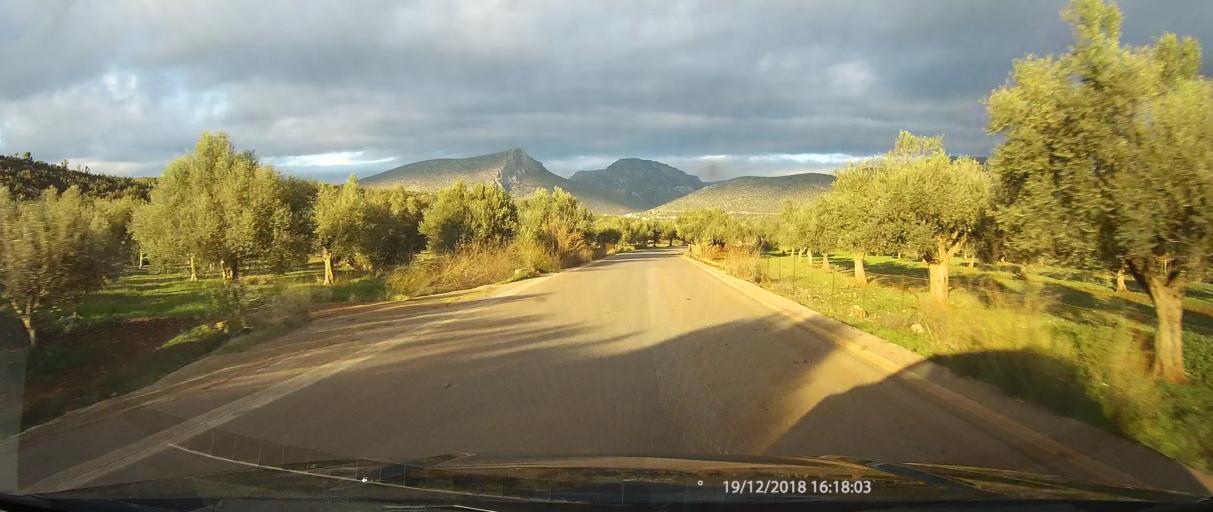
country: GR
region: Peloponnese
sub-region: Nomos Lakonias
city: Kato Glikovrisi
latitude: 36.9188
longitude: 22.8133
